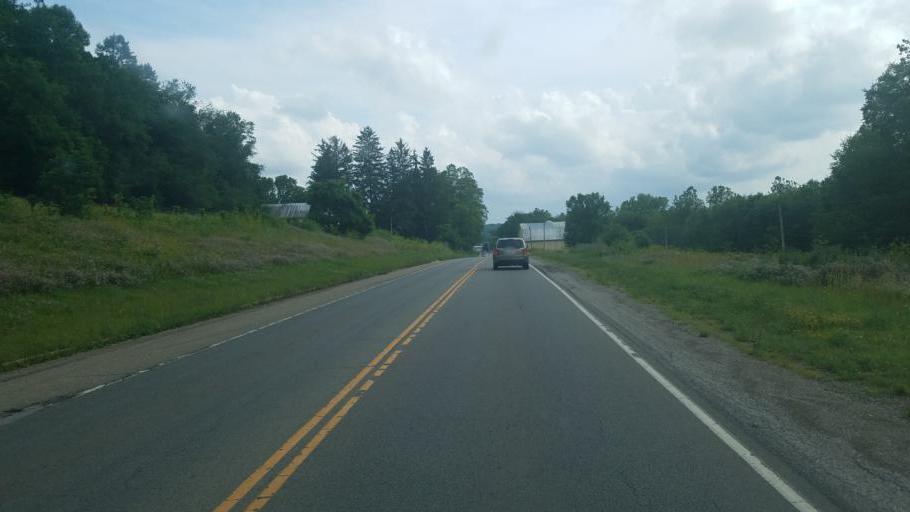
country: US
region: Ohio
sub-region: Richland County
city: Lexington
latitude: 40.7017
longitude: -82.5831
